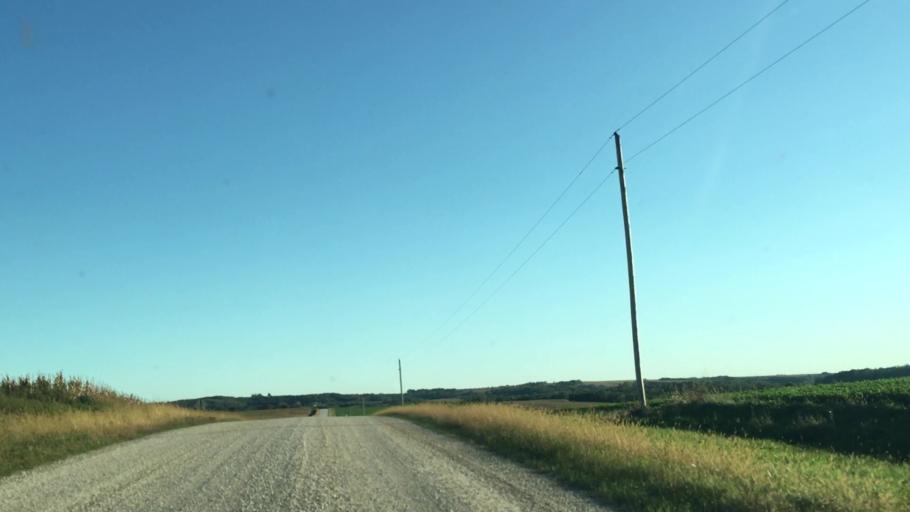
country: US
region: Minnesota
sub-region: Fillmore County
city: Preston
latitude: 43.7745
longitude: -92.0294
